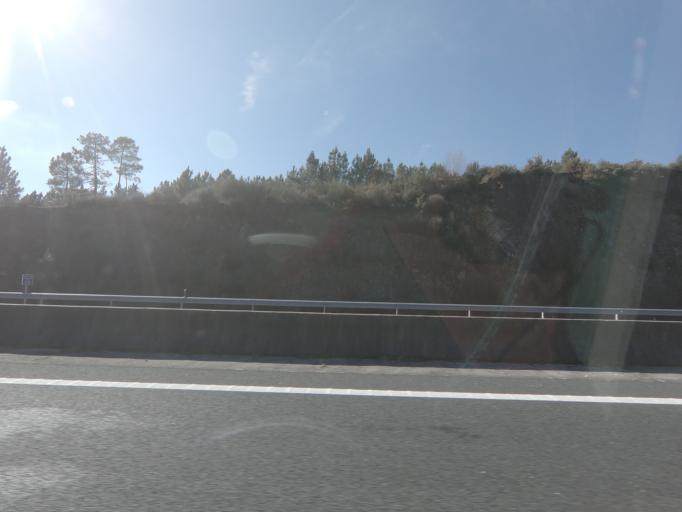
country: ES
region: Galicia
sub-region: Provincia de Ourense
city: Pinor
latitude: 42.4891
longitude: -8.0234
